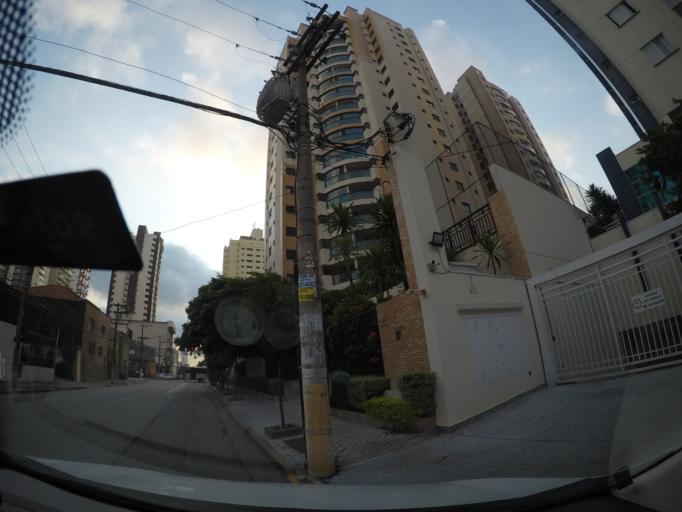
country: BR
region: Sao Paulo
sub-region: Sao Paulo
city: Sao Paulo
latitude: -23.5429
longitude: -46.5663
